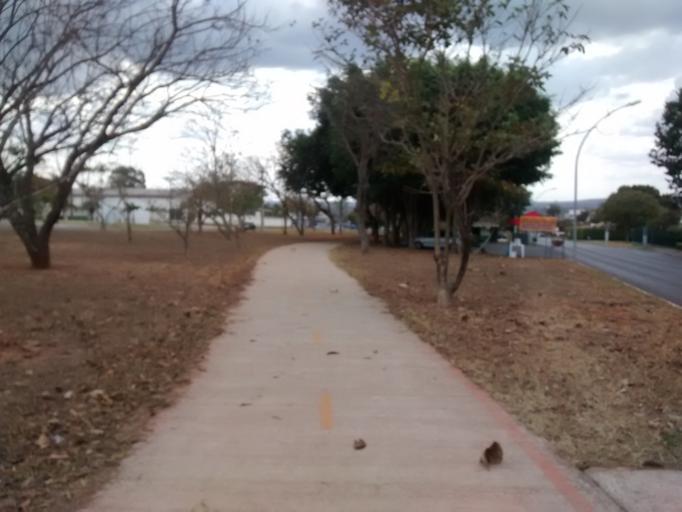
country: BR
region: Federal District
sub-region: Brasilia
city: Brasilia
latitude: -15.7434
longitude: -47.9007
